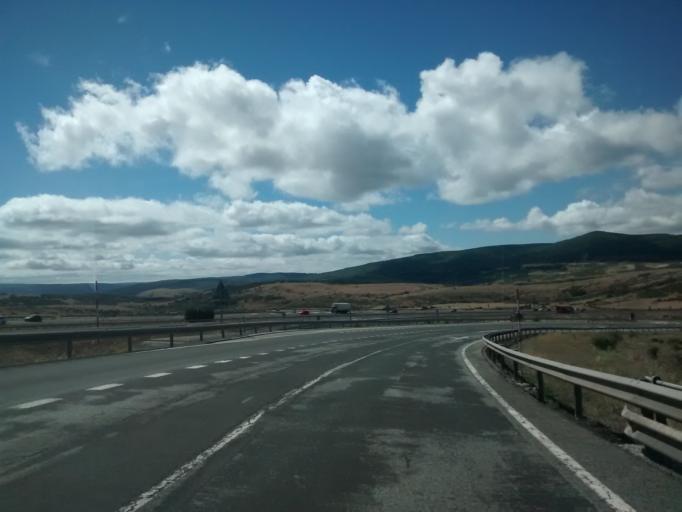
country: ES
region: Cantabria
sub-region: Provincia de Cantabria
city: Mataporquera
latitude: 42.9102
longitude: -4.1176
